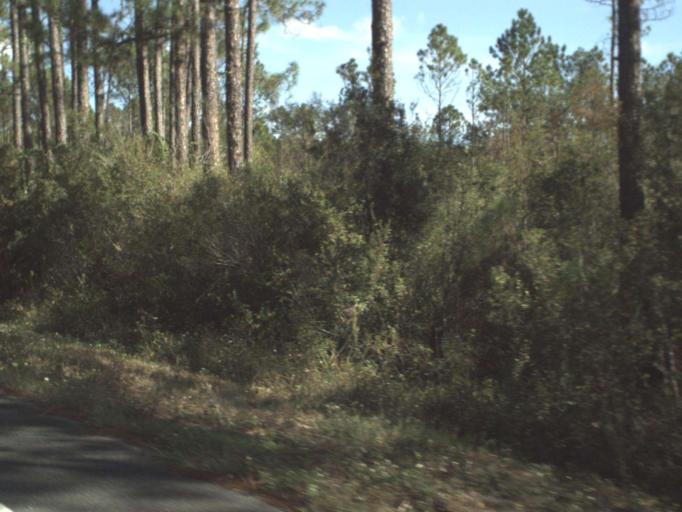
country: US
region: Florida
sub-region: Franklin County
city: Apalachicola
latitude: 29.9000
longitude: -84.9779
